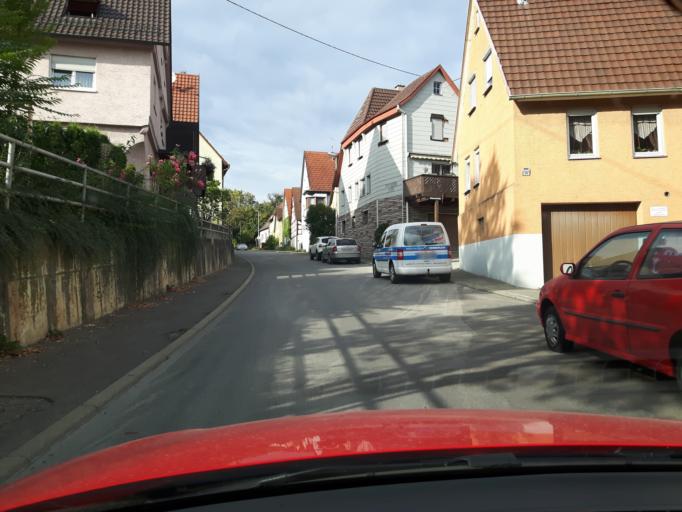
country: DE
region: Baden-Wuerttemberg
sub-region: Regierungsbezirk Stuttgart
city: Nordheim
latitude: 49.0792
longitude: 9.1062
